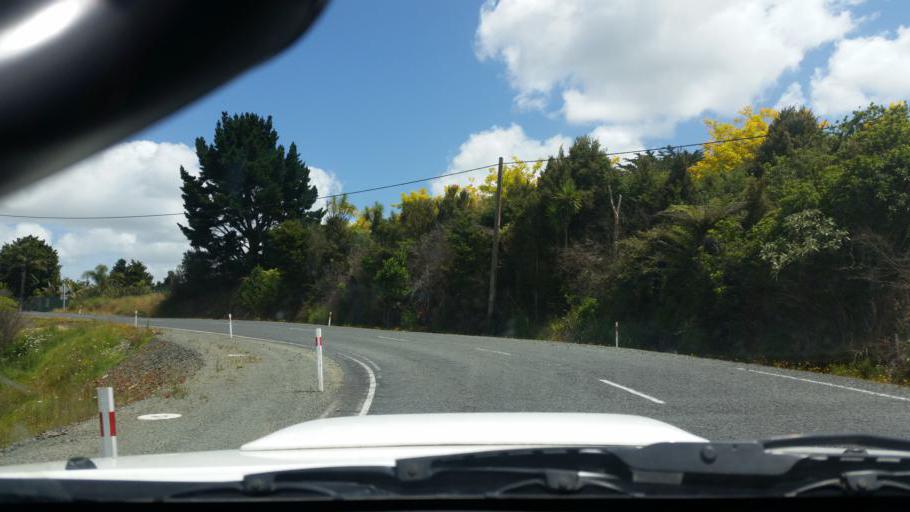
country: NZ
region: Northland
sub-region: Whangarei
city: Ruakaka
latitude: -36.0555
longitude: 174.2725
